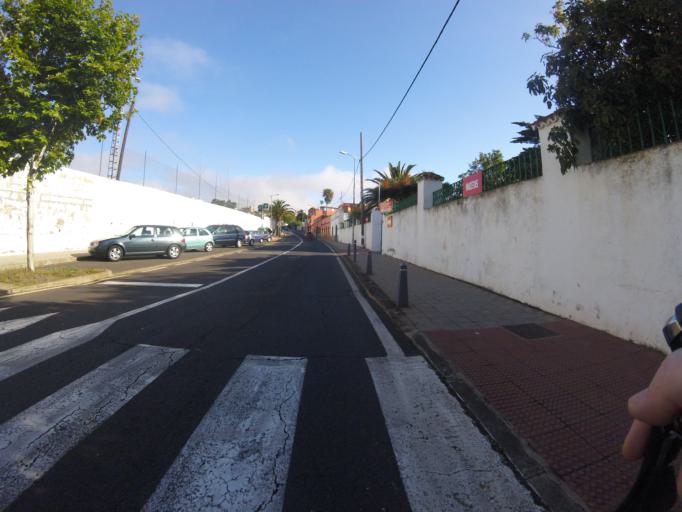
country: ES
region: Canary Islands
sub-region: Provincia de Santa Cruz de Tenerife
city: La Laguna
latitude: 28.4659
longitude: -16.3164
